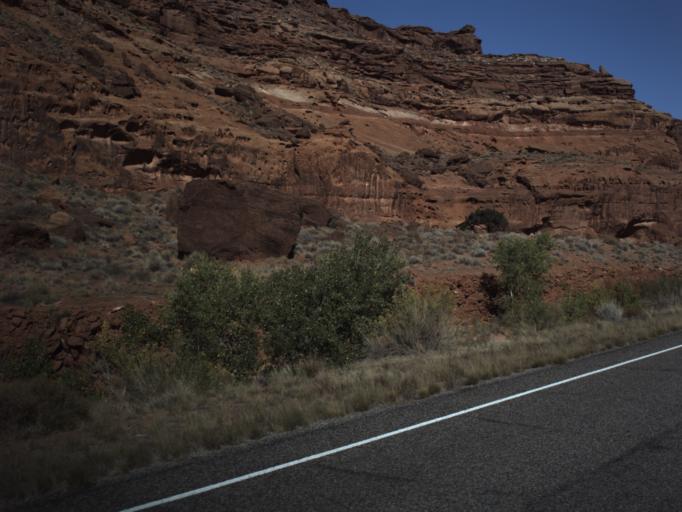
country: US
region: Utah
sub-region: San Juan County
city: Blanding
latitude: 37.9729
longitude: -110.4913
